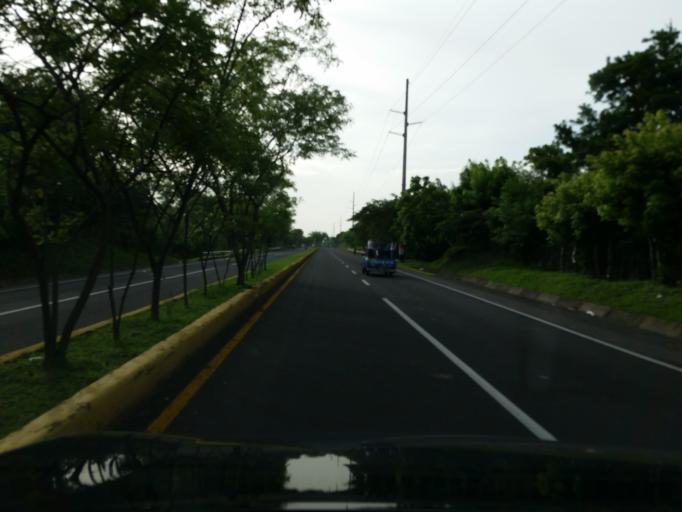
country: NI
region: Granada
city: Granada
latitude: 11.9641
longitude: -86.0090
